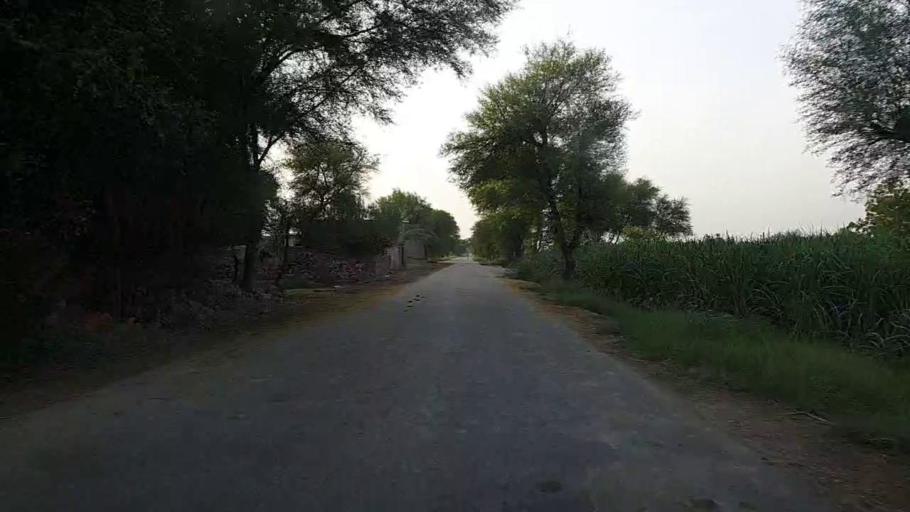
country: PK
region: Sindh
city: Ubauro
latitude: 28.2387
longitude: 69.8129
